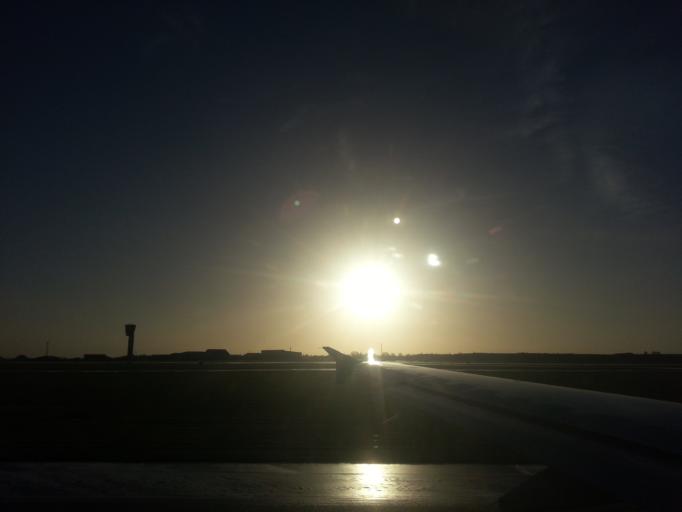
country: DK
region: Capital Region
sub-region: Dragor Kommune
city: Dragor
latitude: 55.6157
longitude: 12.6396
